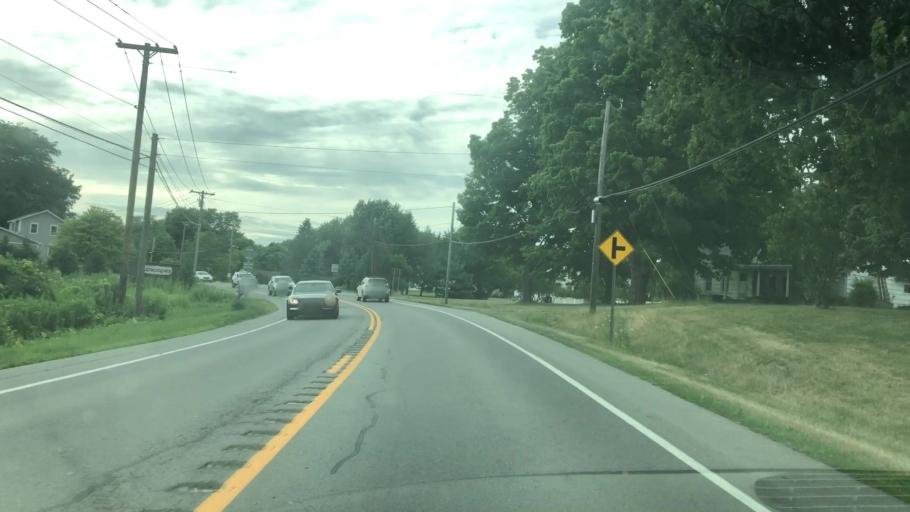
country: US
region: New York
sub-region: Monroe County
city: Fairport
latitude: 43.1302
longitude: -77.4249
